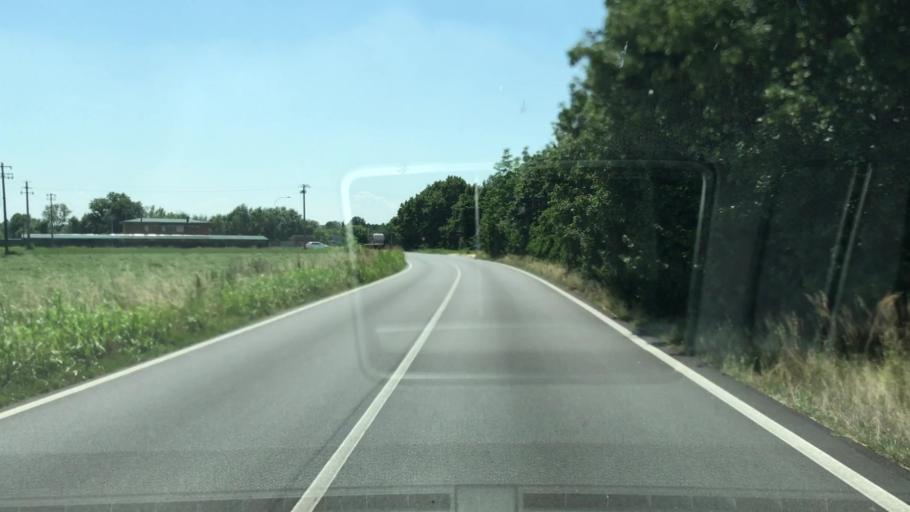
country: IT
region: Lombardy
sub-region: Provincia di Mantova
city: Pegognaga
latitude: 44.9973
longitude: 10.8813
